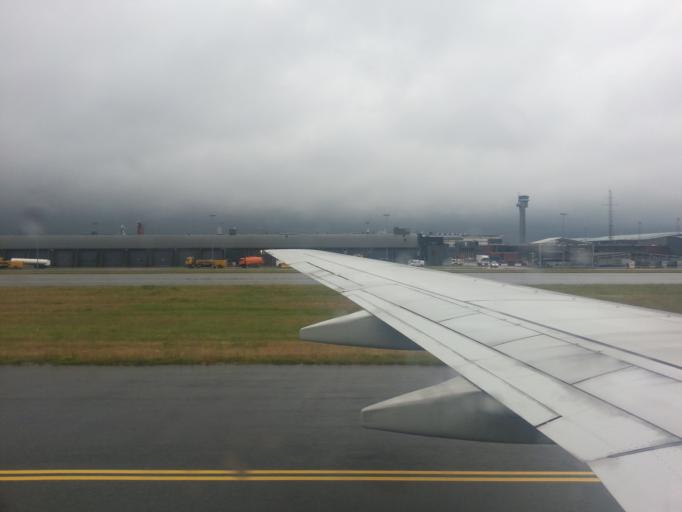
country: NO
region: Akershus
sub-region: Ullensaker
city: Jessheim
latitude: 60.1886
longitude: 11.1110
